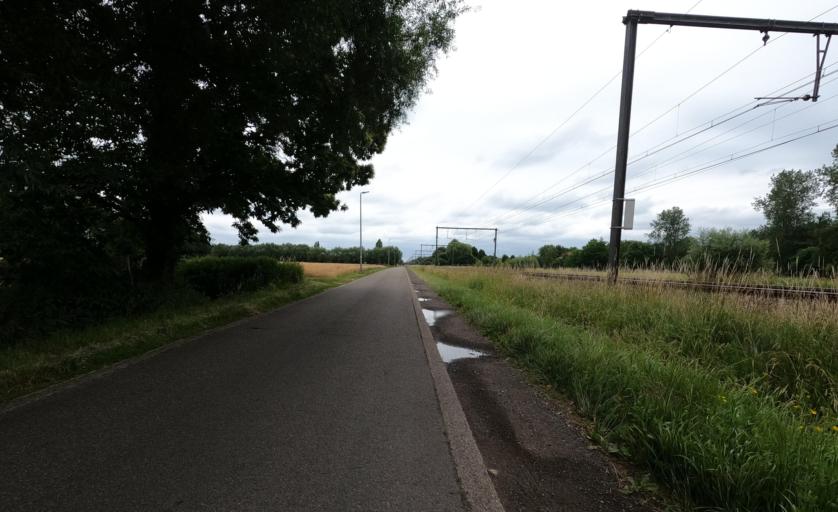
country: BE
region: Flanders
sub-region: Provincie Antwerpen
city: Berlaar
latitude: 51.0919
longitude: 4.6773
